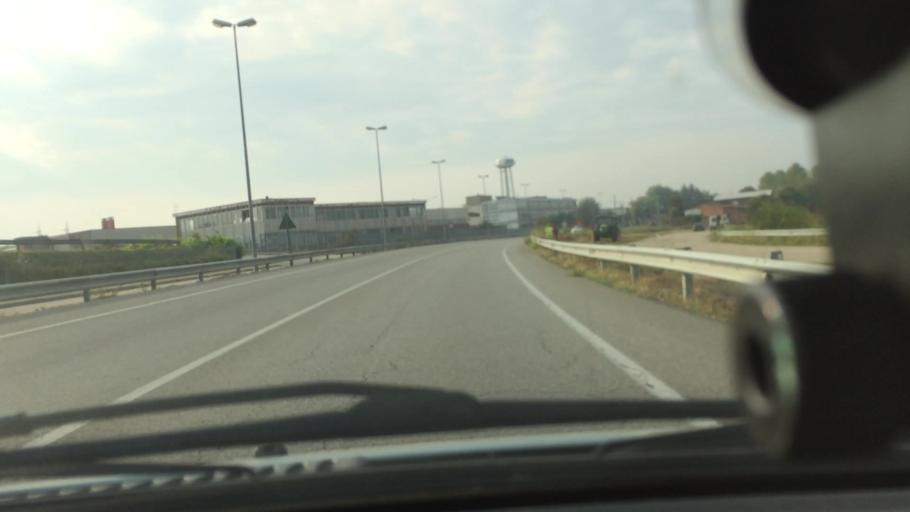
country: IT
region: Piedmont
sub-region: Provincia di Torino
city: Villastellone
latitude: 44.9155
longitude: 7.7429
